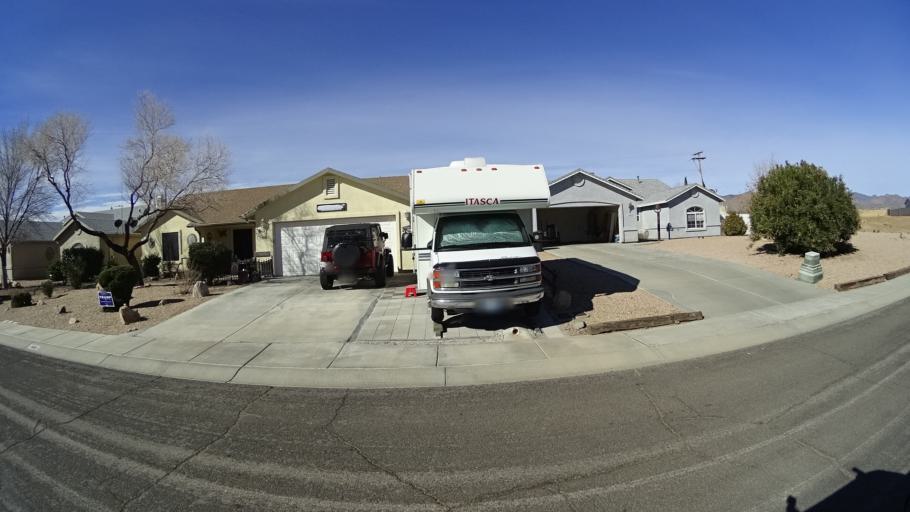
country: US
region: Arizona
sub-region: Mohave County
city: New Kingman-Butler
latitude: 35.2702
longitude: -114.0255
